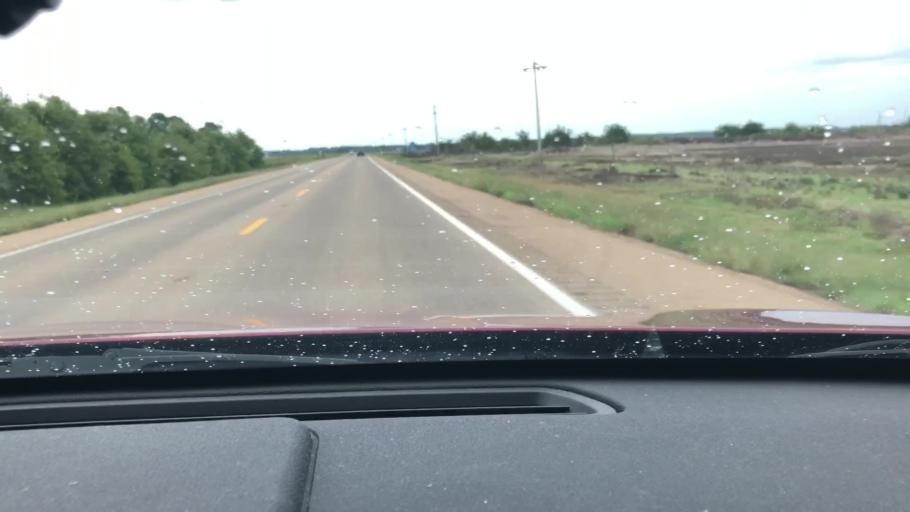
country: US
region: Arkansas
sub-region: Lafayette County
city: Lewisville
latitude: 33.4119
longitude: -93.7721
